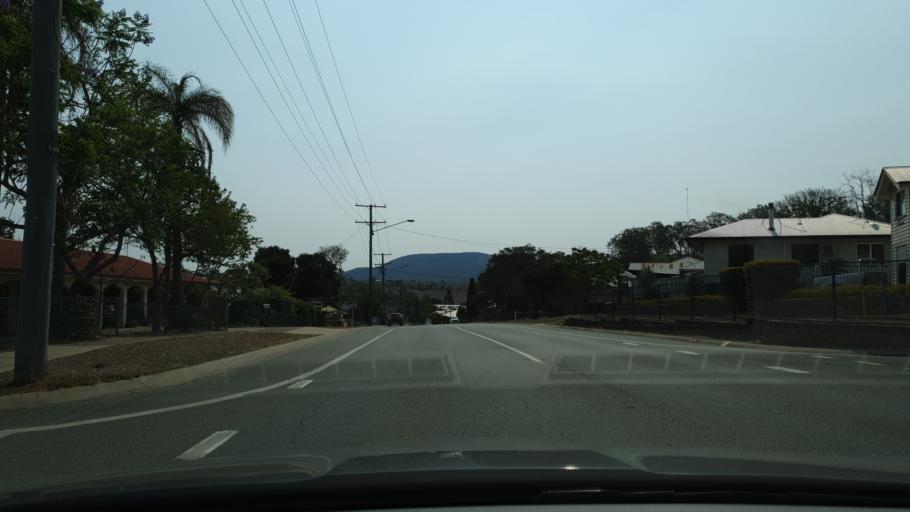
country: AU
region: Queensland
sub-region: Ipswich
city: Deebing Heights
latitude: -27.9924
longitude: 152.6879
